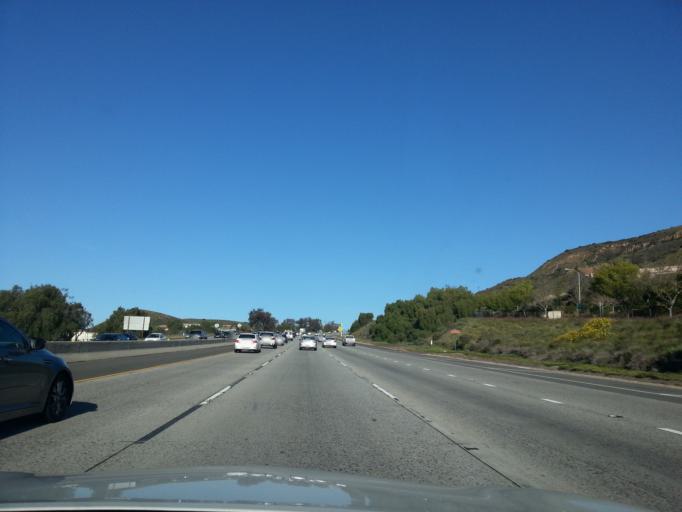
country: US
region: California
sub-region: Ventura County
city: Casa Conejo
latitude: 34.1921
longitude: -118.9444
